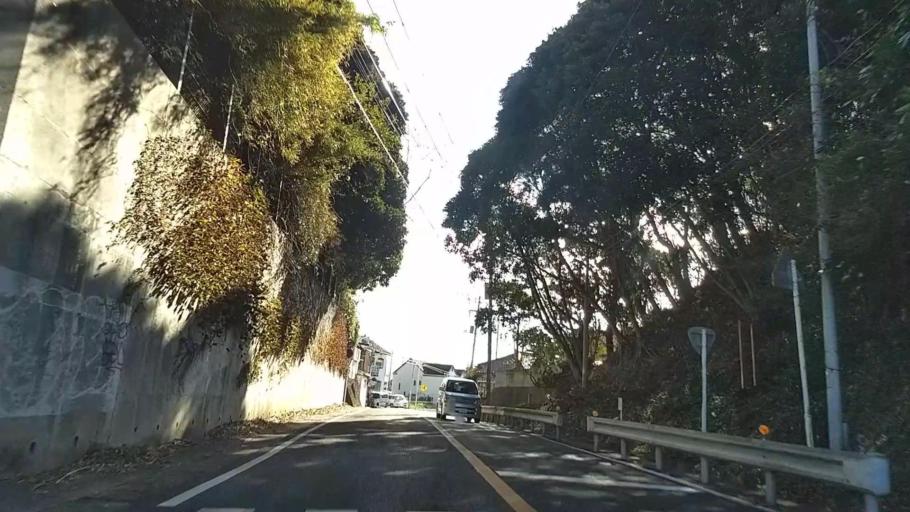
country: JP
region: Chiba
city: Tateyama
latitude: 35.0494
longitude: 139.8339
